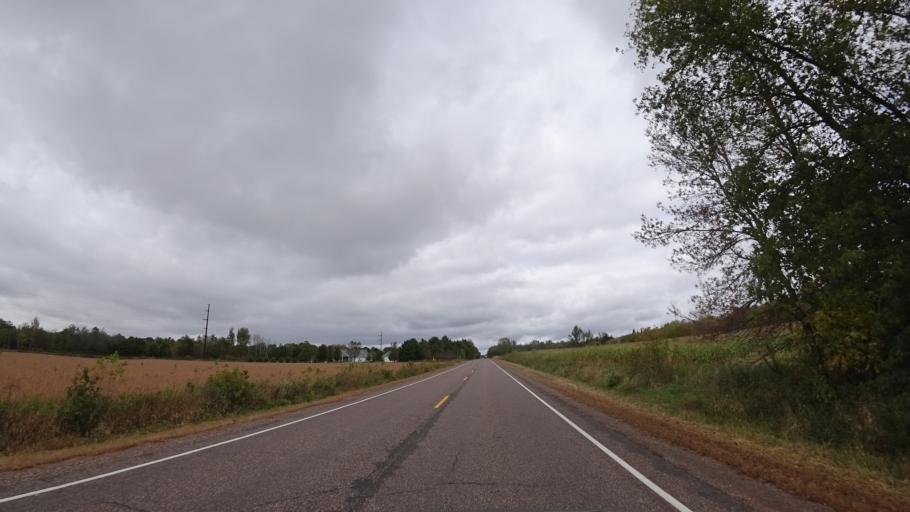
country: US
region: Wisconsin
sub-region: Chippewa County
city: Lake Wissota
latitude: 45.0166
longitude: -91.2867
